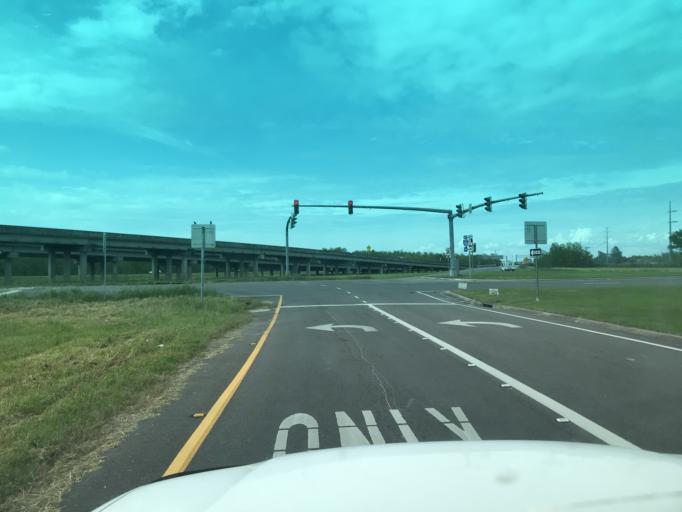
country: US
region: Louisiana
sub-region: Saint Bernard Parish
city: Chalmette
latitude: 30.0434
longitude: -89.9382
